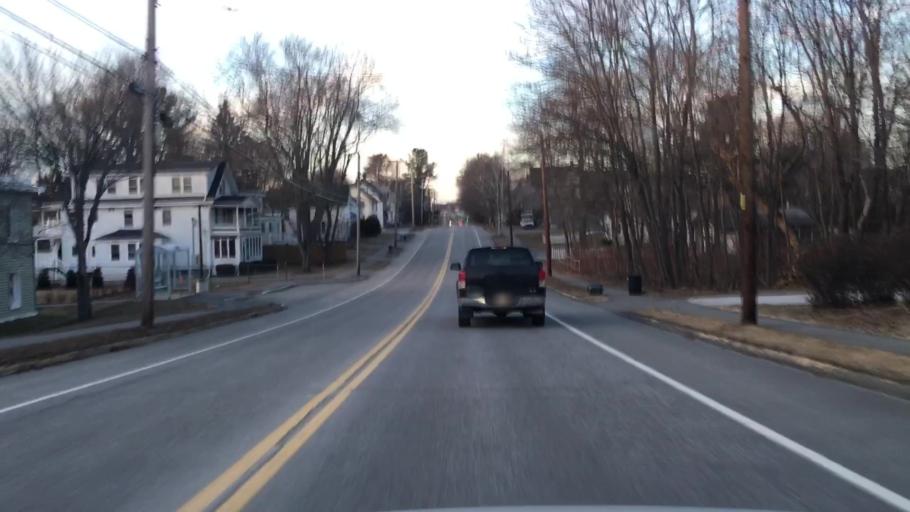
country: US
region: Maine
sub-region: Penobscot County
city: Brewer
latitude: 44.7918
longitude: -68.7574
